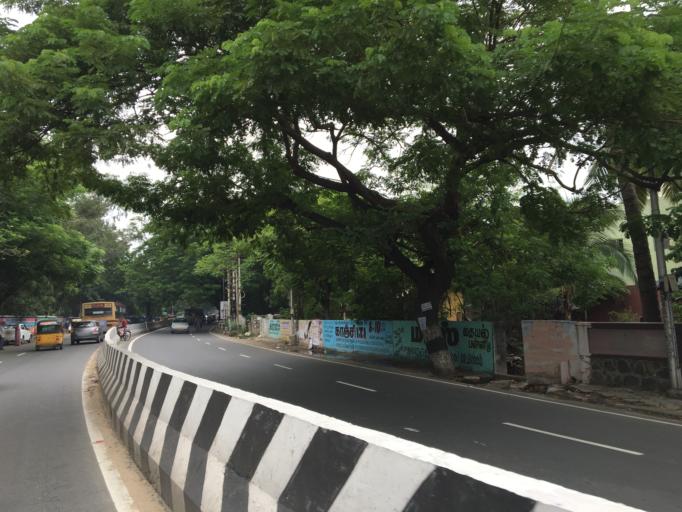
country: IN
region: Tamil Nadu
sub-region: Kancheepuram
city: Alandur
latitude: 12.9952
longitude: 80.2170
